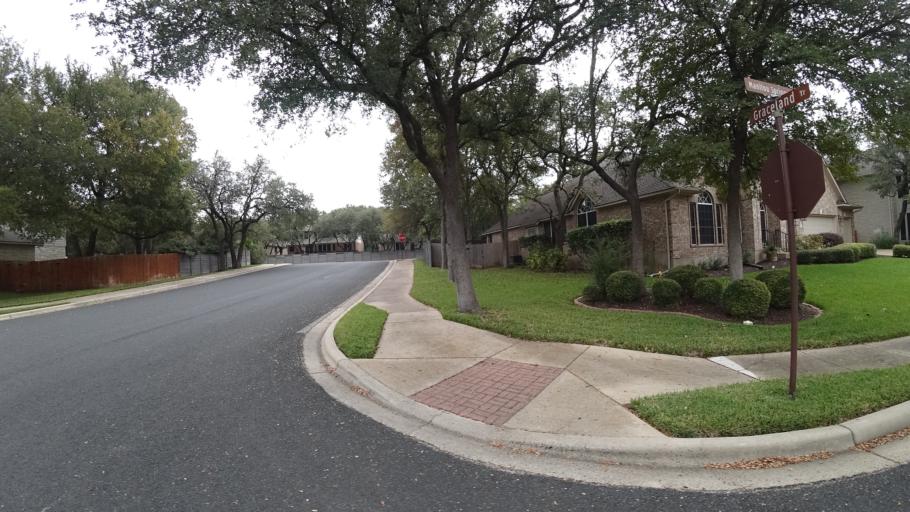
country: US
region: Texas
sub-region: Williamson County
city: Brushy Creek
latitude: 30.5140
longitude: -97.7460
